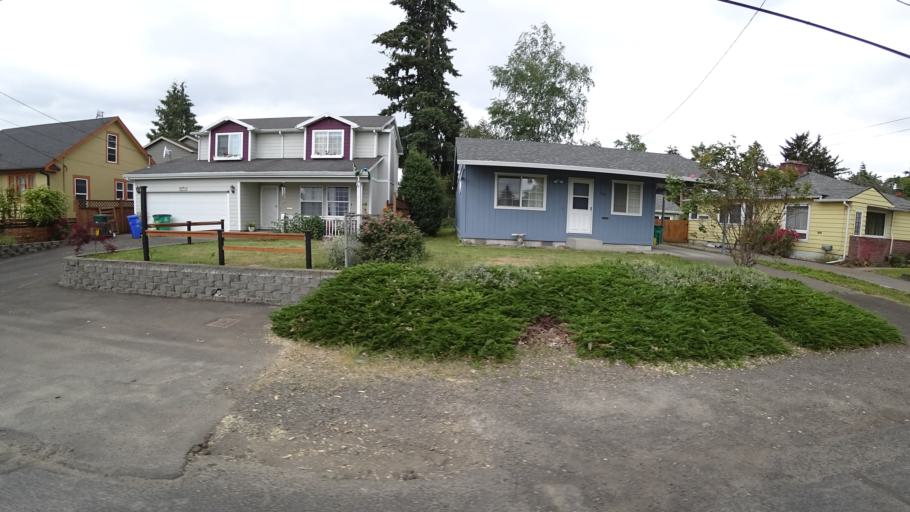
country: US
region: Oregon
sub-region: Multnomah County
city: Lents
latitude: 45.4749
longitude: -122.5830
